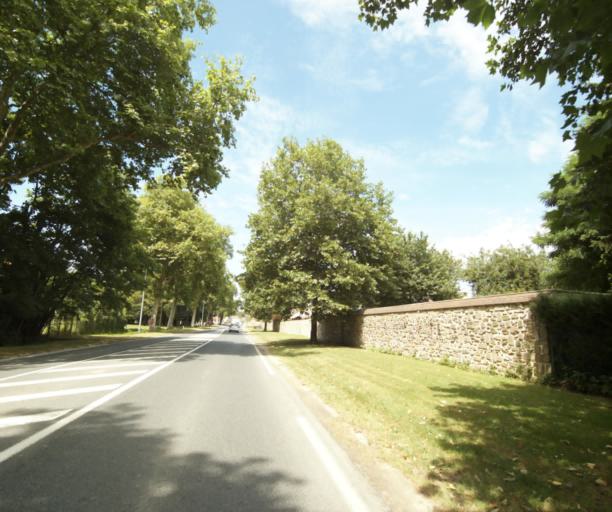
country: FR
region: Ile-de-France
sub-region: Departement de Seine-et-Marne
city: Chailly-en-Biere
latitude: 48.4628
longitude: 2.6079
